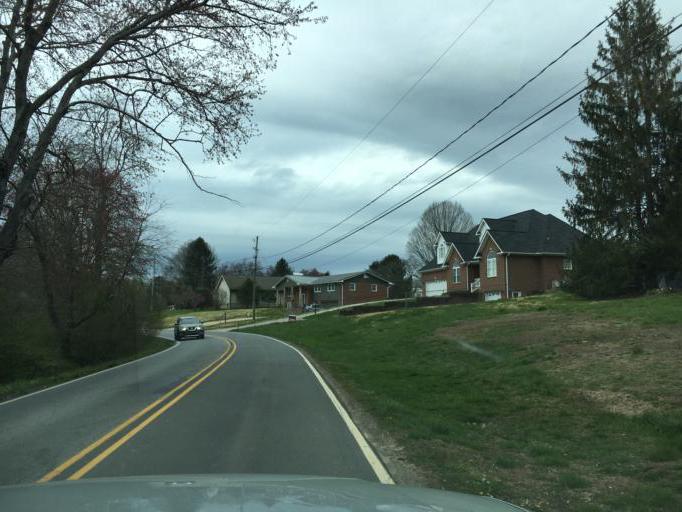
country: US
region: North Carolina
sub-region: Transylvania County
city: Brevard
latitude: 35.2375
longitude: -82.7192
